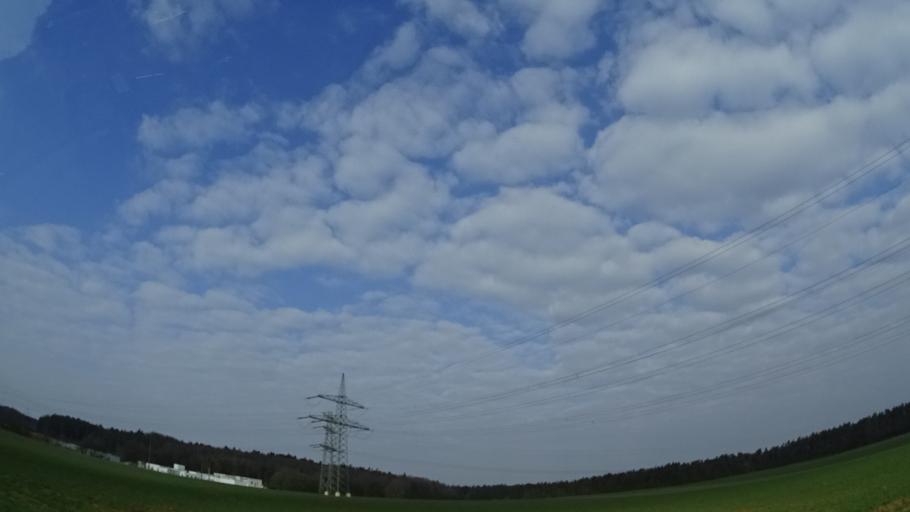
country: DE
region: Bavaria
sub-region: Regierungsbezirk Mittelfranken
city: Altdorf
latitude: 49.3975
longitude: 11.3322
